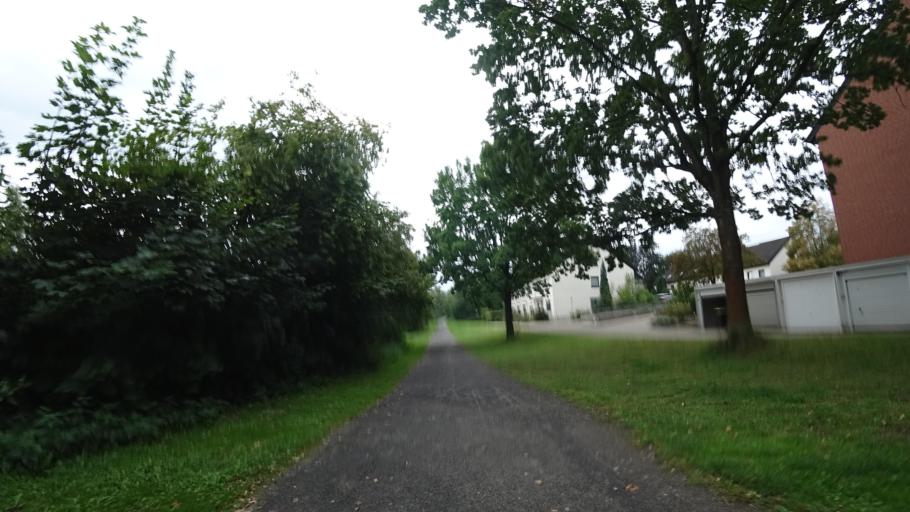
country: DE
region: North Rhine-Westphalia
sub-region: Regierungsbezirk Detmold
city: Bielefeld
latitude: 52.0450
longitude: 8.5523
